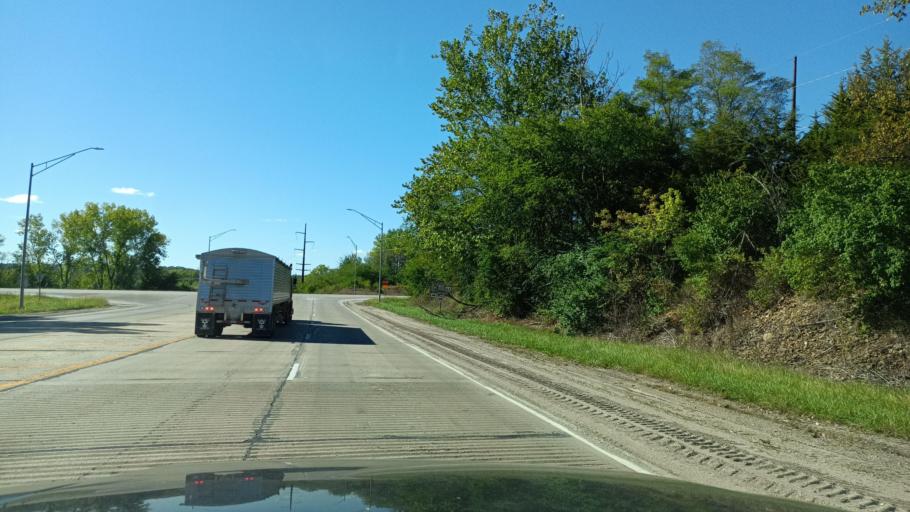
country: US
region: Illinois
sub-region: Hancock County
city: Warsaw
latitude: 40.3904
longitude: -91.4282
